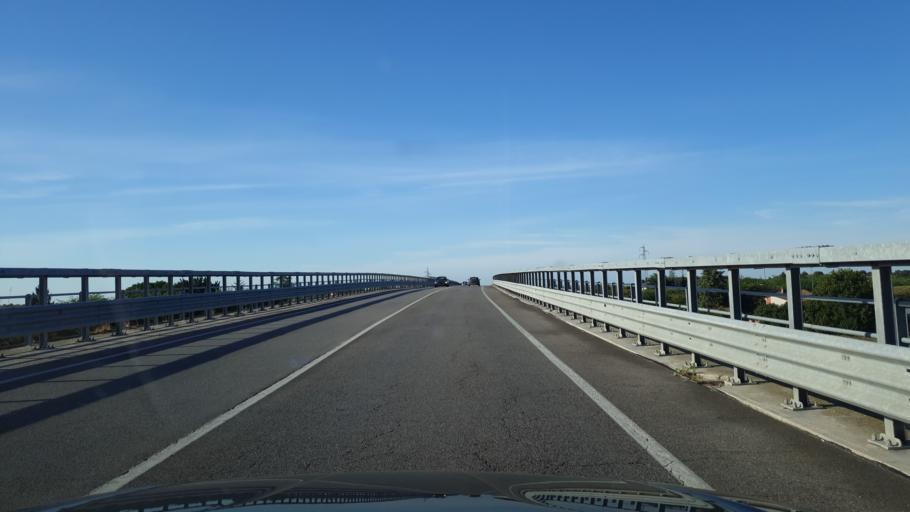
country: IT
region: Emilia-Romagna
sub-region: Provincia di Ravenna
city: Alfonsine
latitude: 44.5061
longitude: 12.0604
